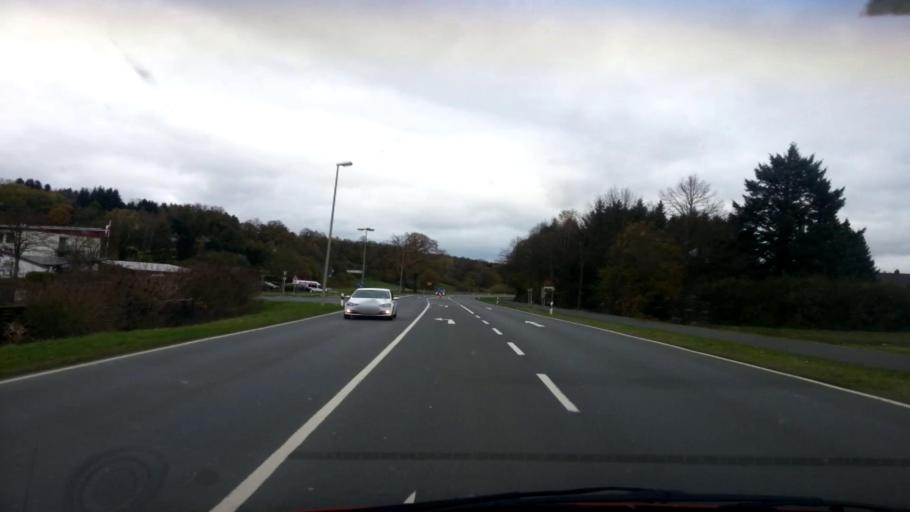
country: DE
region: Bavaria
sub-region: Upper Franconia
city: Kronach
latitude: 50.2455
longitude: 11.3358
